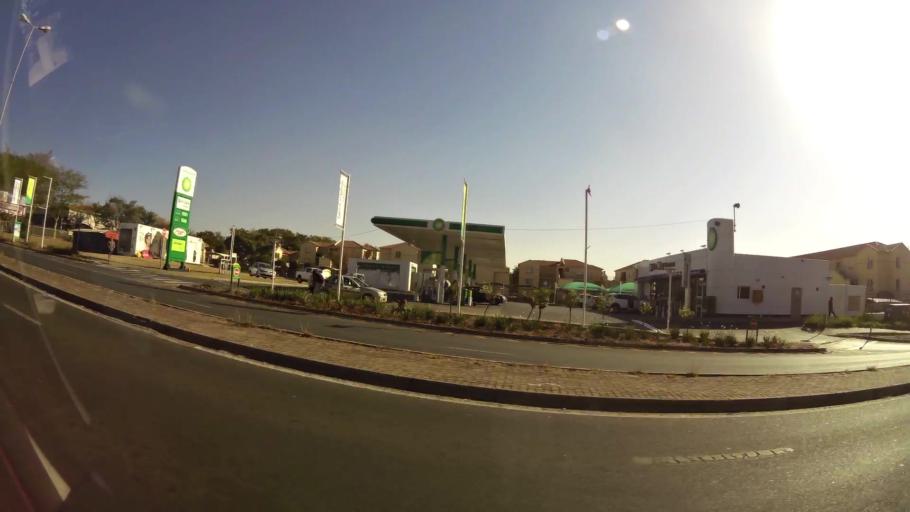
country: ZA
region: Gauteng
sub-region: City of Tshwane Metropolitan Municipality
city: Pretoria
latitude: -25.7306
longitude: 28.2459
